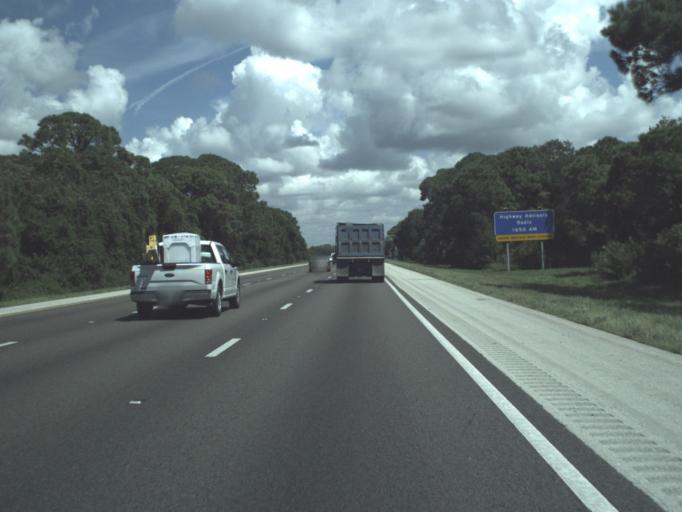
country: US
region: Florida
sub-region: Sarasota County
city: Bee Ridge
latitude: 27.2430
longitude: -82.4506
